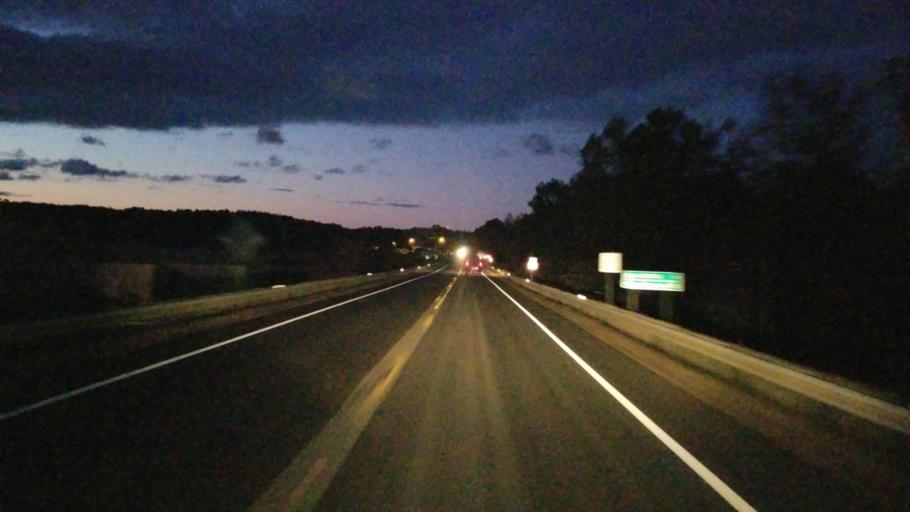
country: US
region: Ohio
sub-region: Vinton County
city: McArthur
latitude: 39.2909
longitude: -82.4674
